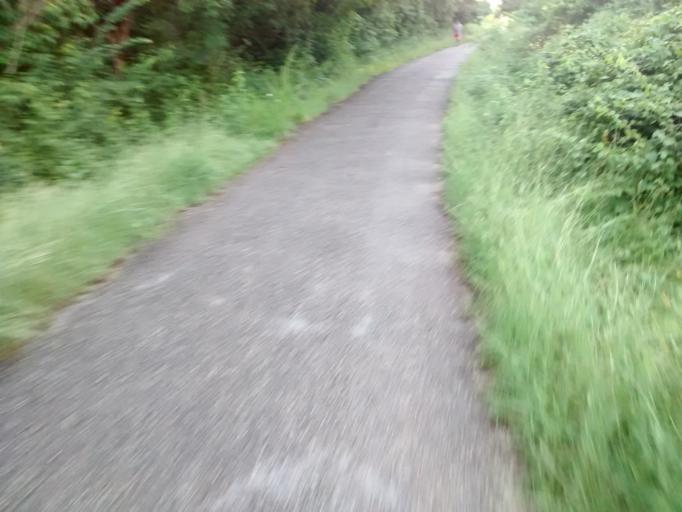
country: MX
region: Yucatan
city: Valladolid
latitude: 20.7146
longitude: -88.2209
